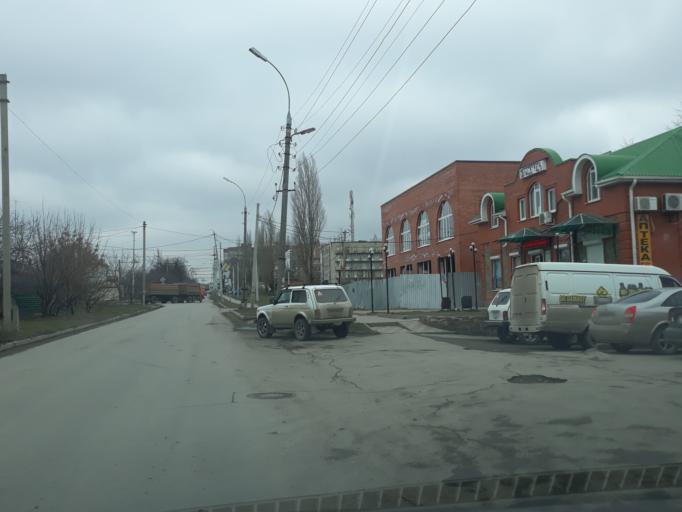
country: RU
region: Rostov
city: Taganrog
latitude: 47.2714
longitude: 38.9305
